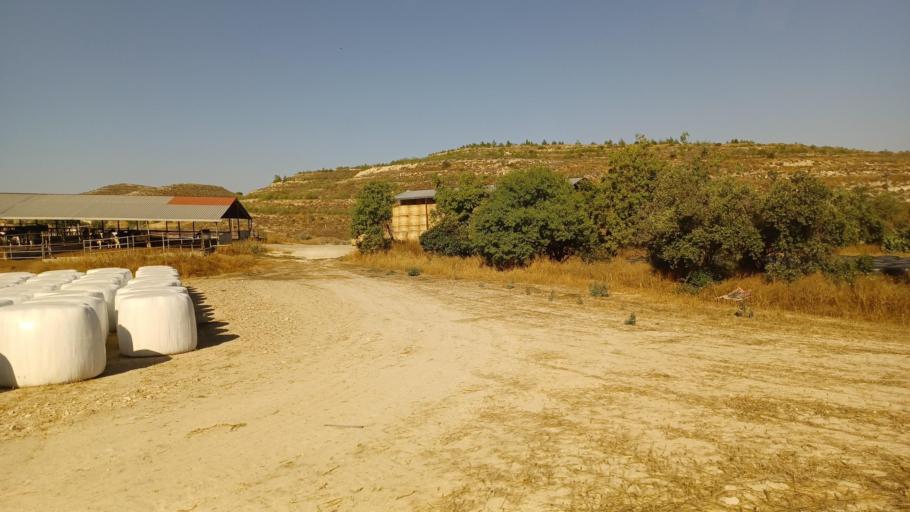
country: CY
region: Larnaka
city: Athienou
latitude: 35.0277
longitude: 33.5420
